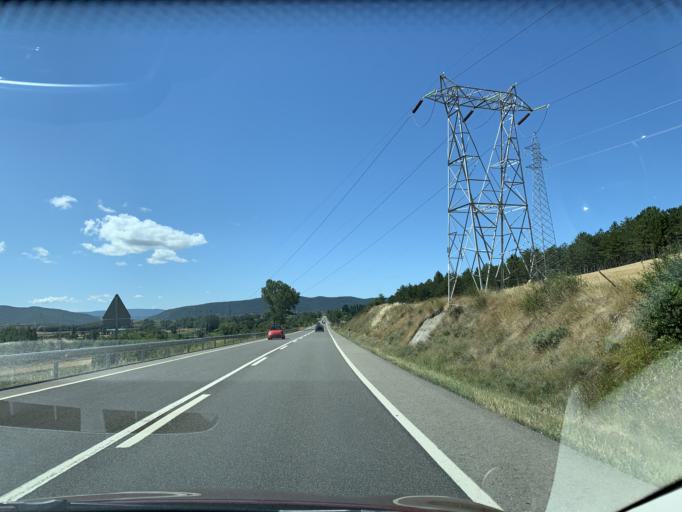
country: ES
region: Aragon
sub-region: Provincia de Huesca
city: Sabinanigo
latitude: 42.5622
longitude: -0.3305
